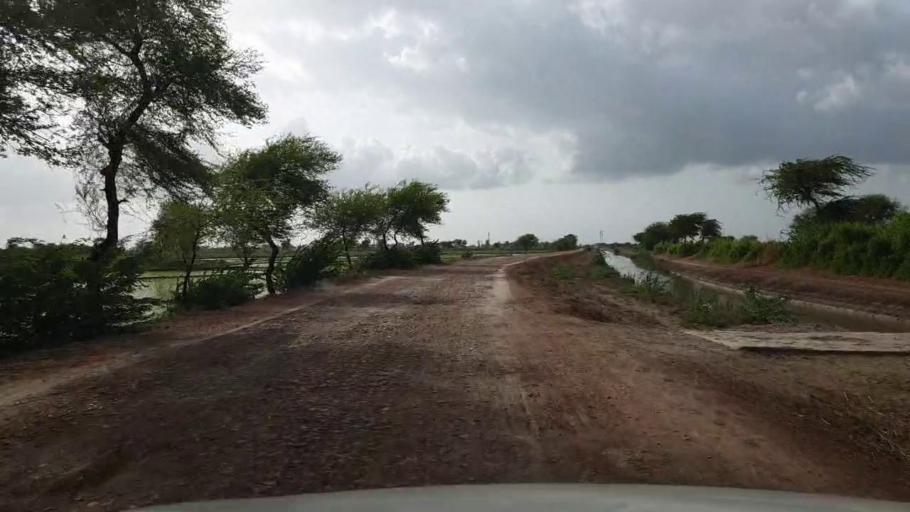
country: PK
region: Sindh
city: Kario
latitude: 24.7891
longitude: 68.5812
